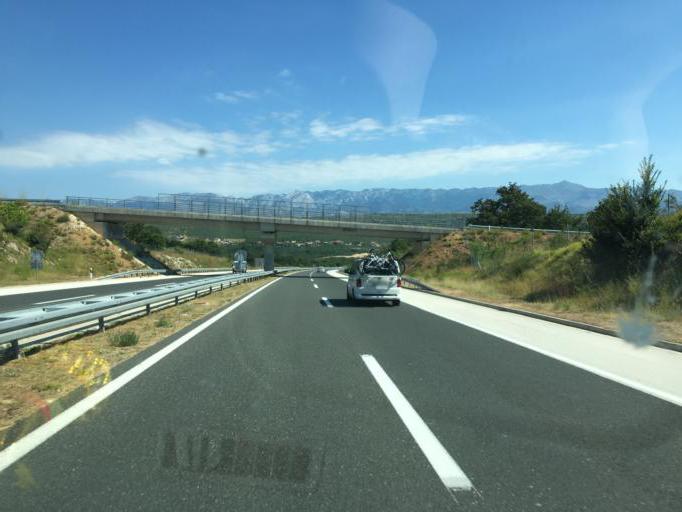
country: HR
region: Zadarska
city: Posedarje
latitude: 44.2061
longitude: 15.4448
